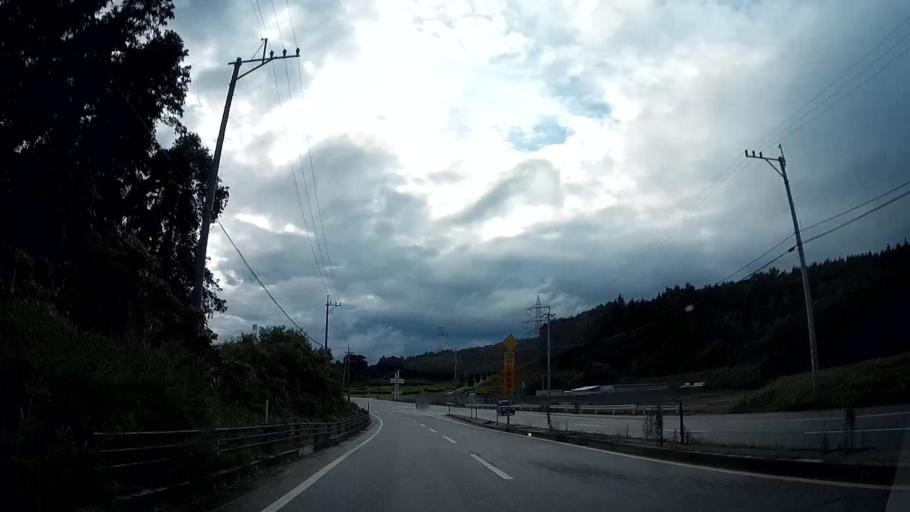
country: JP
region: Kumamoto
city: Ozu
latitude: 32.8756
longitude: 130.9297
